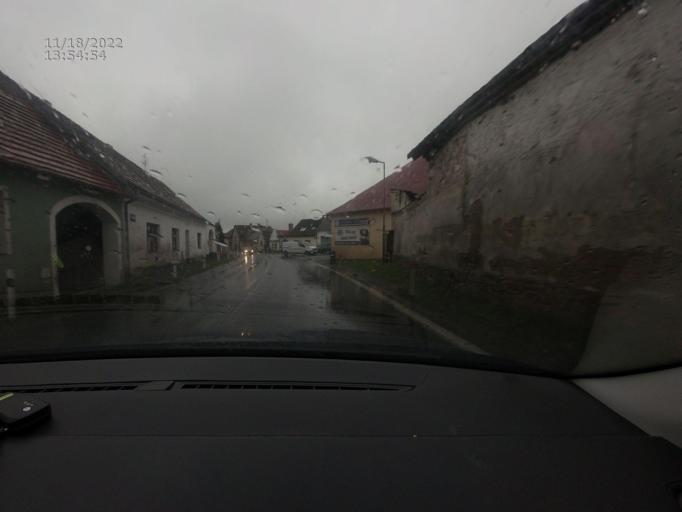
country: CZ
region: Jihocesky
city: Sedlice
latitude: 49.3792
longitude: 13.9345
